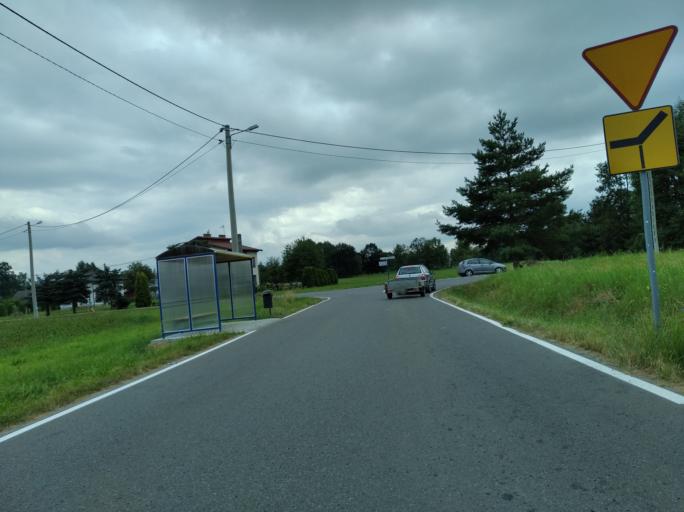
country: PL
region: Subcarpathian Voivodeship
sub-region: Powiat krosnienski
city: Odrzykon
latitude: 49.7406
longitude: 21.7317
